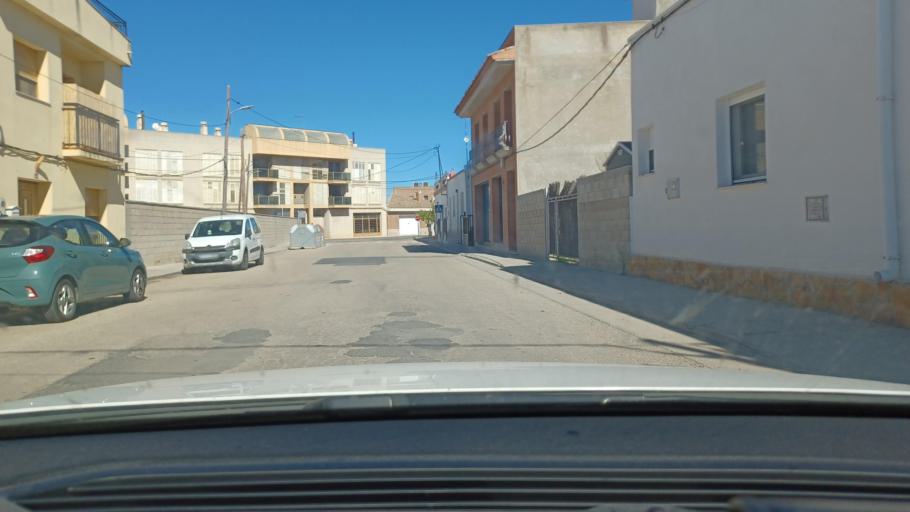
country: ES
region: Catalonia
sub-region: Provincia de Tarragona
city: Deltebre
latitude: 40.7198
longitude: 0.7394
